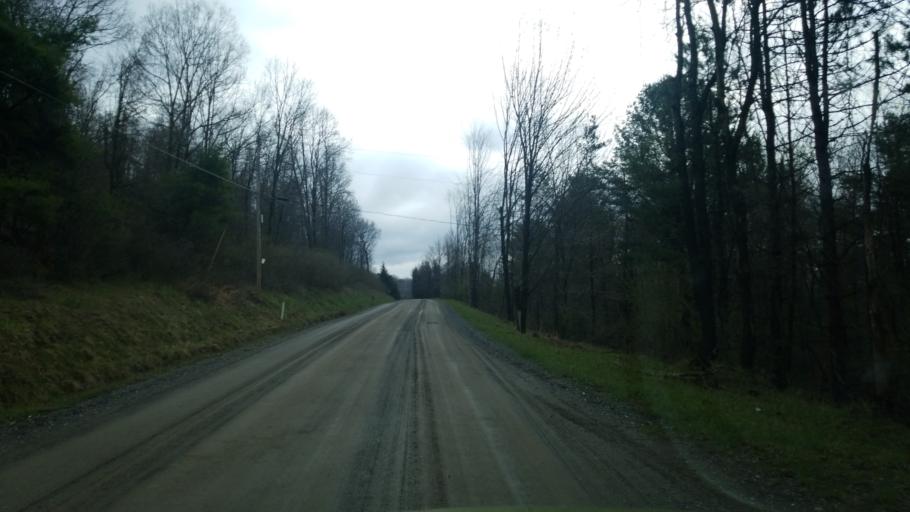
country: US
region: Pennsylvania
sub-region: Clearfield County
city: Shiloh
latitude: 41.1251
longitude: -78.3372
